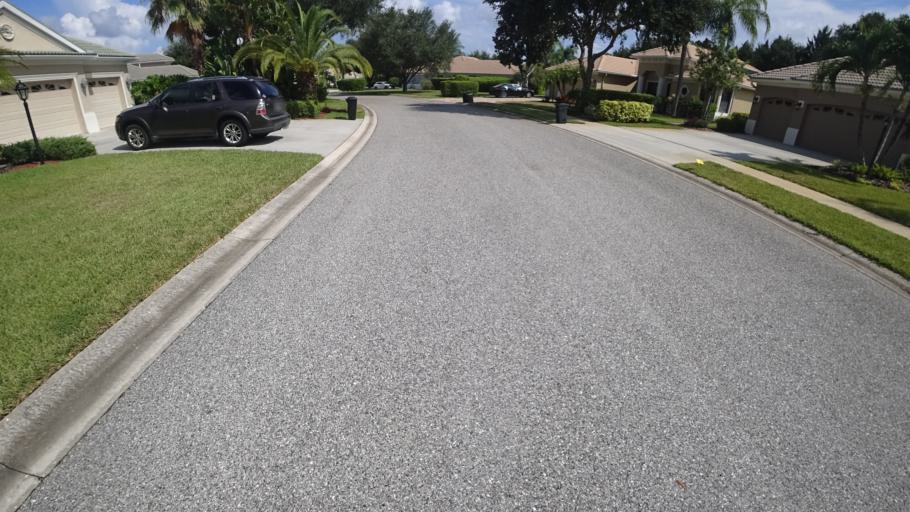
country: US
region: Florida
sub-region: Sarasota County
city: The Meadows
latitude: 27.4165
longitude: -82.4187
